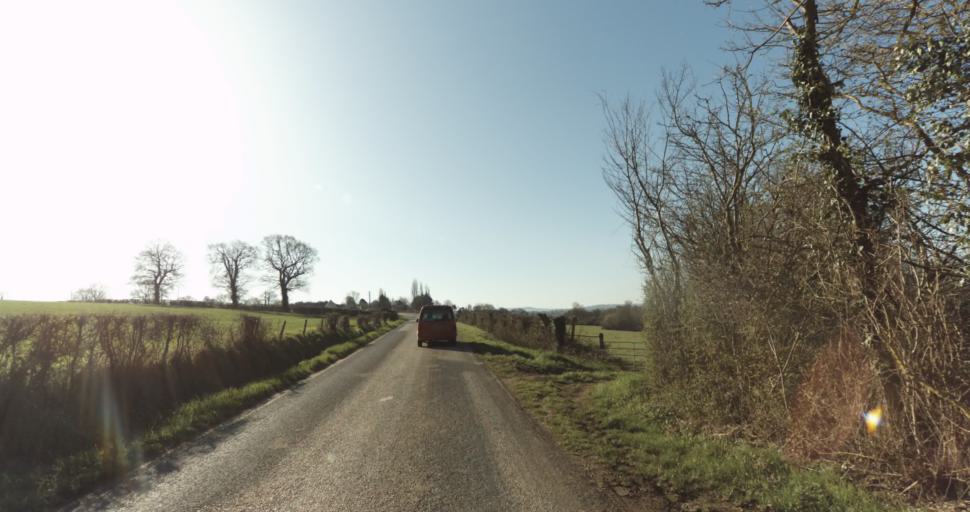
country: FR
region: Lower Normandy
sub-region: Departement du Calvados
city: Saint-Pierre-sur-Dives
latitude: 49.0098
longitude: -0.0180
